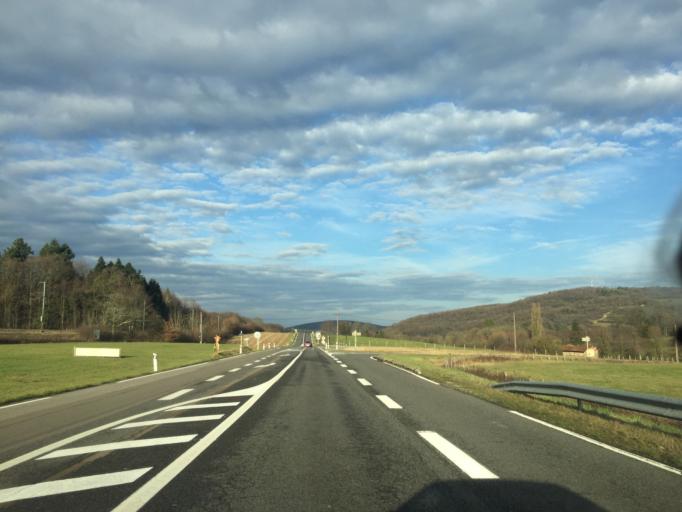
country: FR
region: Franche-Comte
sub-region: Departement du Jura
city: Mouchard
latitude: 46.9446
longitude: 5.7805
